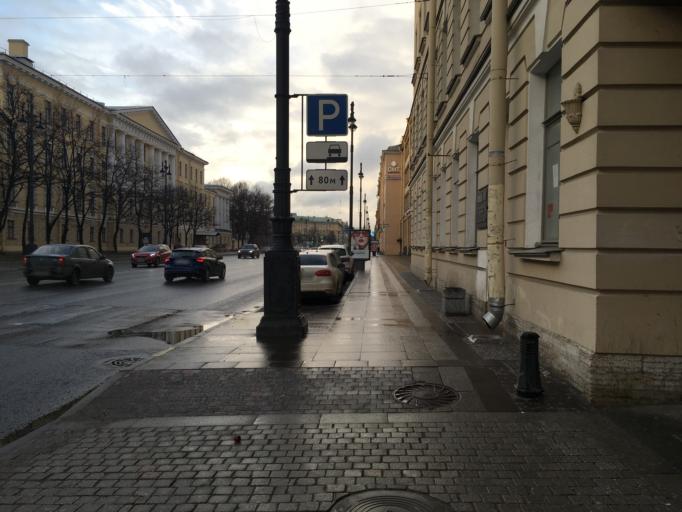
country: RU
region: St.-Petersburg
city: Saint Petersburg
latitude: 59.9187
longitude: 30.3181
